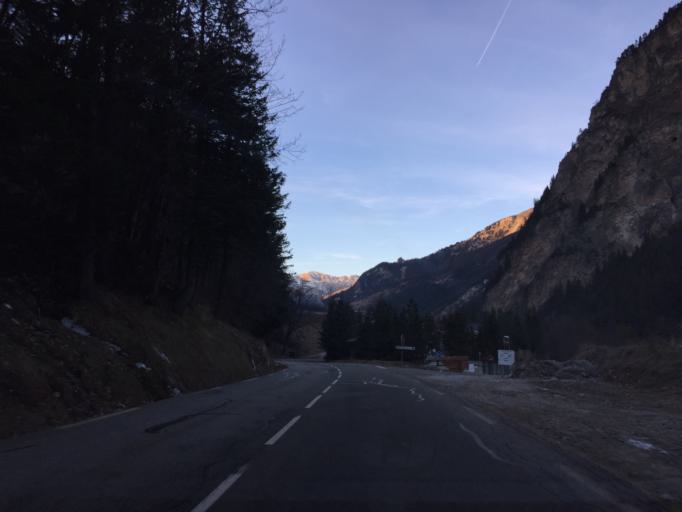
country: FR
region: Rhone-Alpes
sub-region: Departement de la Savoie
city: Courchevel
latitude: 45.3961
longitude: 6.7098
